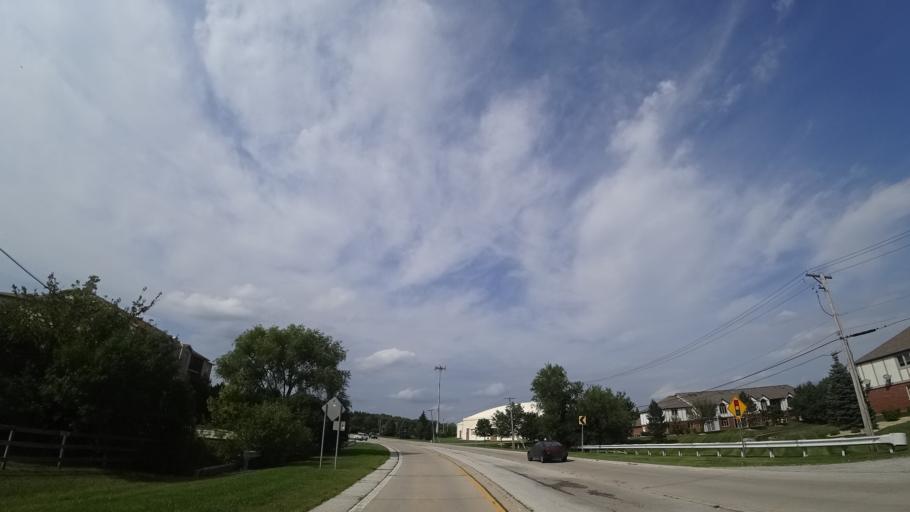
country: US
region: Illinois
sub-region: Cook County
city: Tinley Park
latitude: 41.5566
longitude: -87.7714
